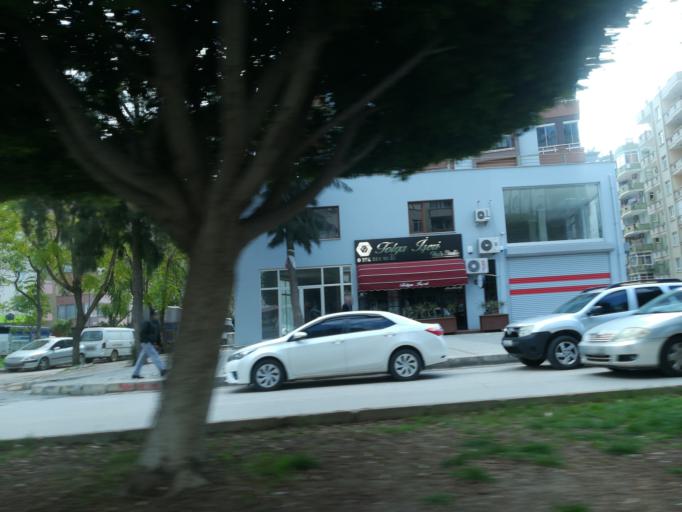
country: TR
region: Adana
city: Adana
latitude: 37.0311
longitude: 35.3014
